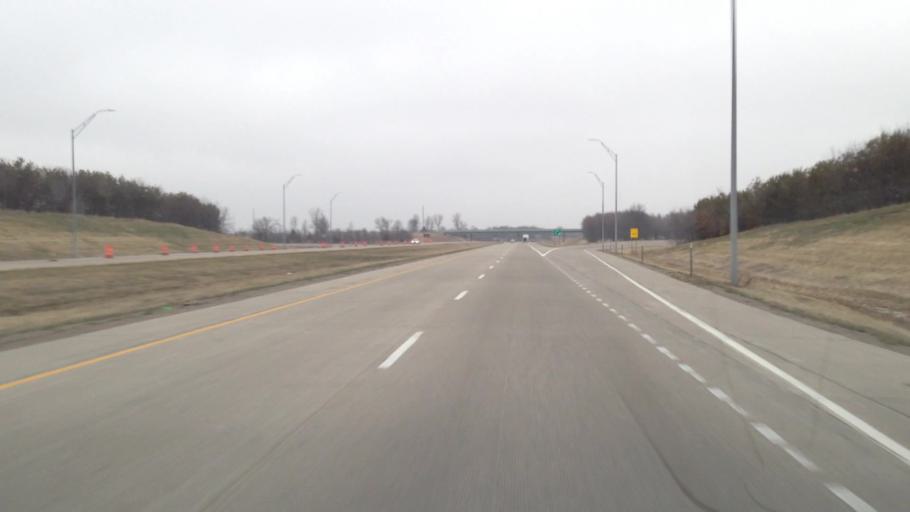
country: US
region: Iowa
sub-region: Decatur County
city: Leon
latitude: 40.7331
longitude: -93.8431
